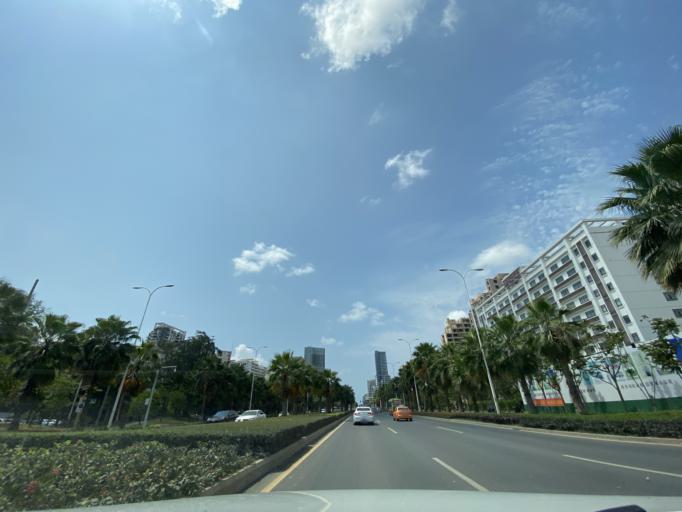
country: CN
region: Hainan
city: Sanya
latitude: 18.2814
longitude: 109.5139
